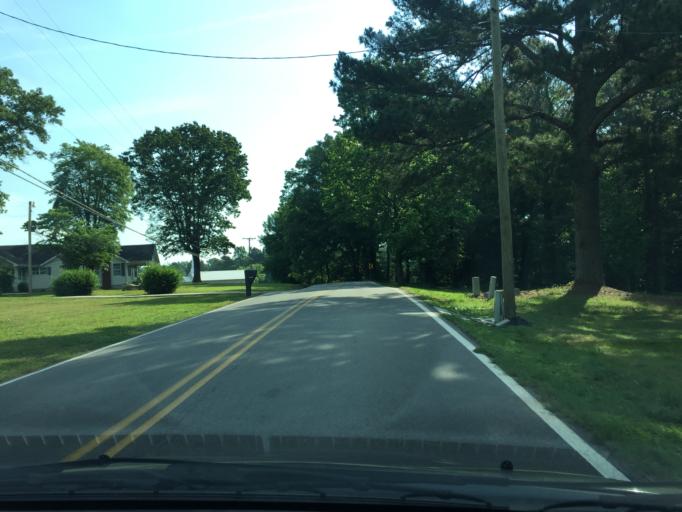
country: US
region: Tennessee
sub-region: Hamilton County
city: Collegedale
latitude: 35.0611
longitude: -85.0135
